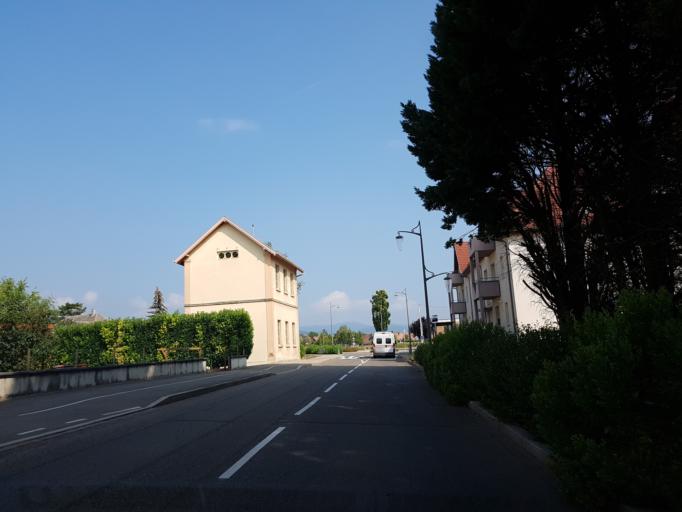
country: FR
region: Alsace
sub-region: Departement du Haut-Rhin
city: Eguisheim
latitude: 48.0451
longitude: 7.3107
